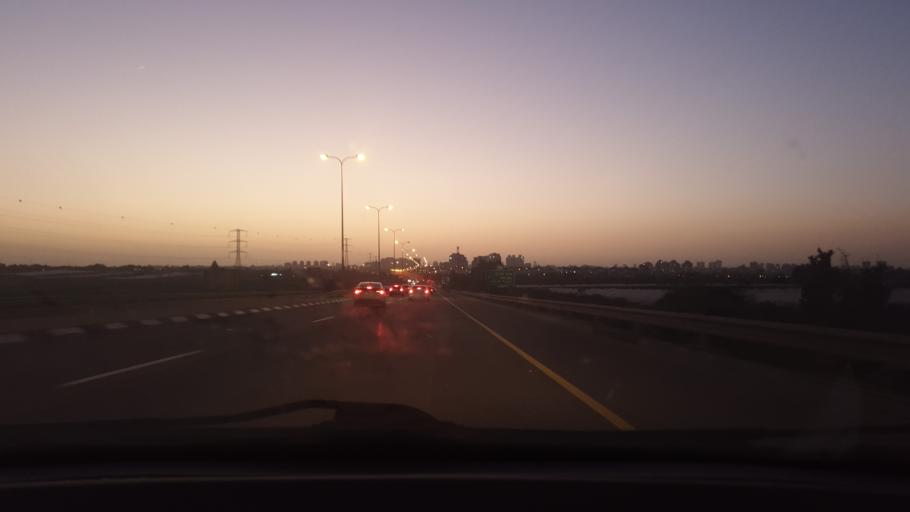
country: IL
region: Central District
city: Nehalim
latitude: 32.0682
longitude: 34.9313
